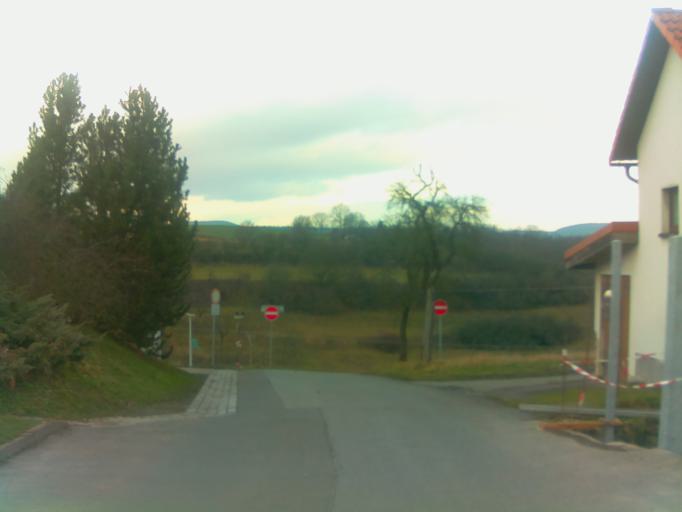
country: DE
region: Thuringia
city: Rudolstadt
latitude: 50.6975
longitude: 11.3451
